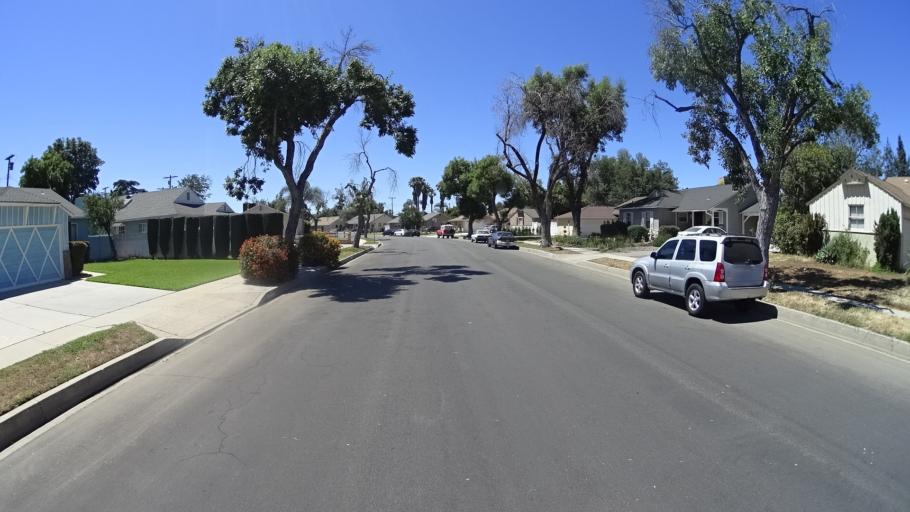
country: US
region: California
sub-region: Los Angeles County
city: San Fernando
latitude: 34.2592
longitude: -118.4704
